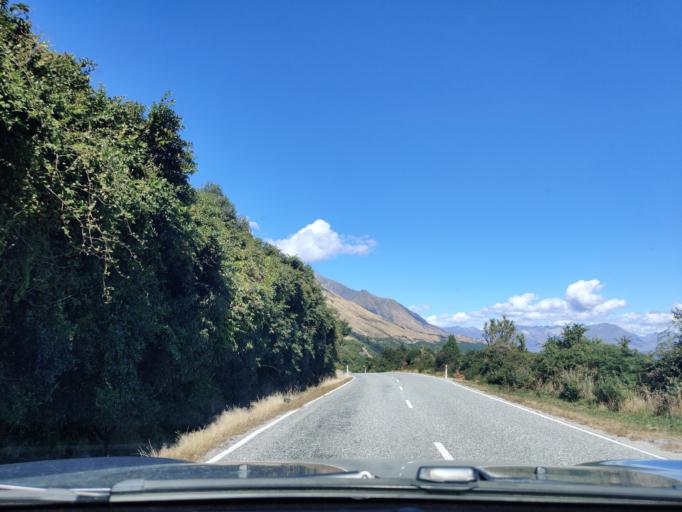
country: NZ
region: Otago
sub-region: Queenstown-Lakes District
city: Queenstown
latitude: -44.9418
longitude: 168.4319
